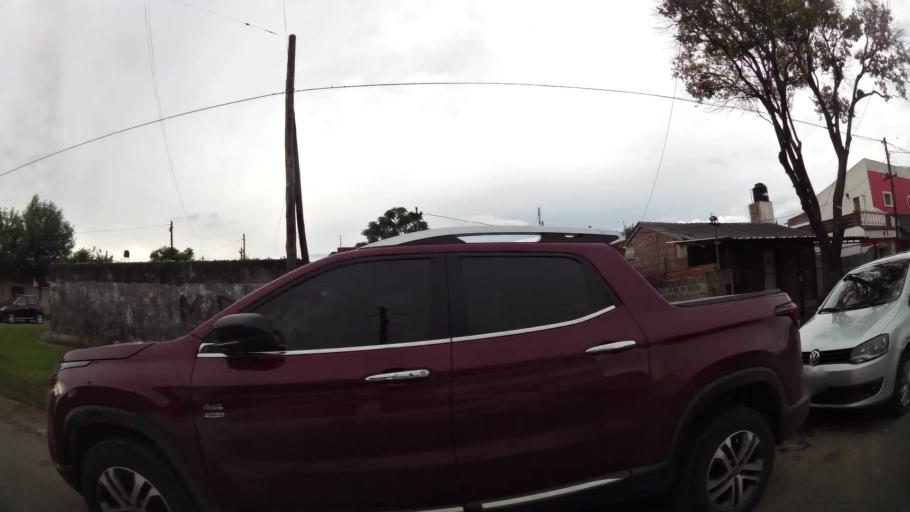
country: AR
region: Santa Fe
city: Gobernador Galvez
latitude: -32.9984
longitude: -60.6702
